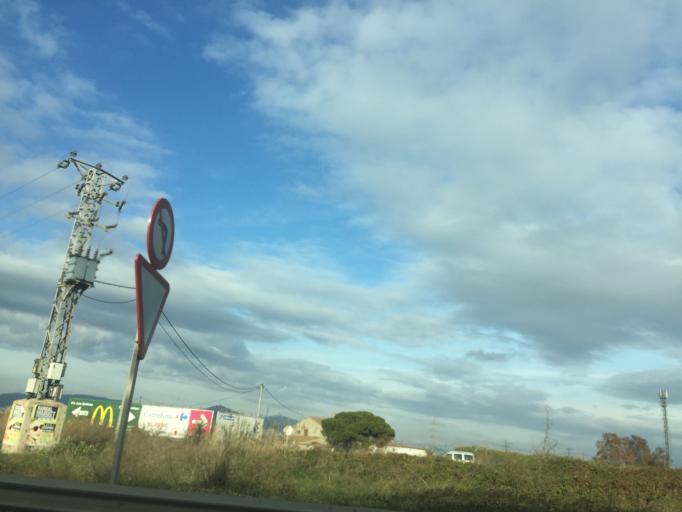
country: ES
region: Catalonia
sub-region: Provincia de Barcelona
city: El Prat de Llobregat
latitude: 41.3309
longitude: 2.0801
